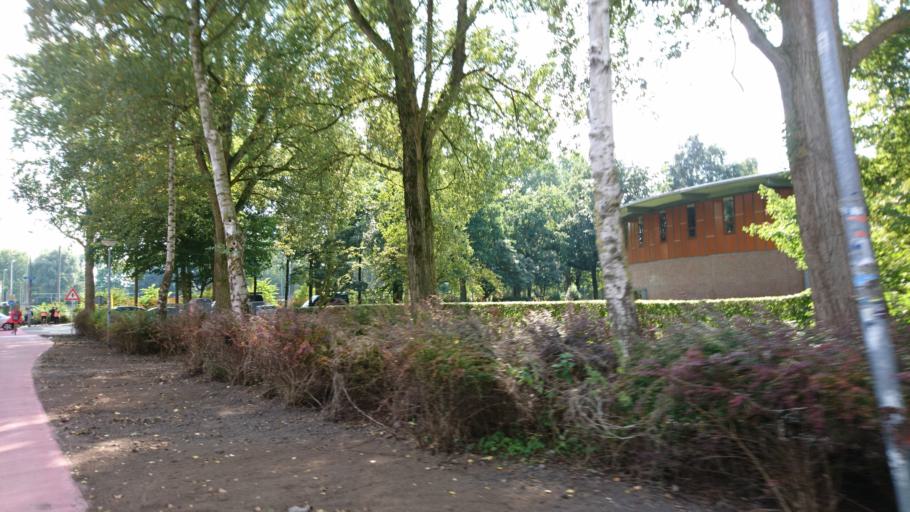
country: NL
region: Groningen
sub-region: Gemeente Groningen
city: Korrewegwijk
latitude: 53.2322
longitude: 6.5469
